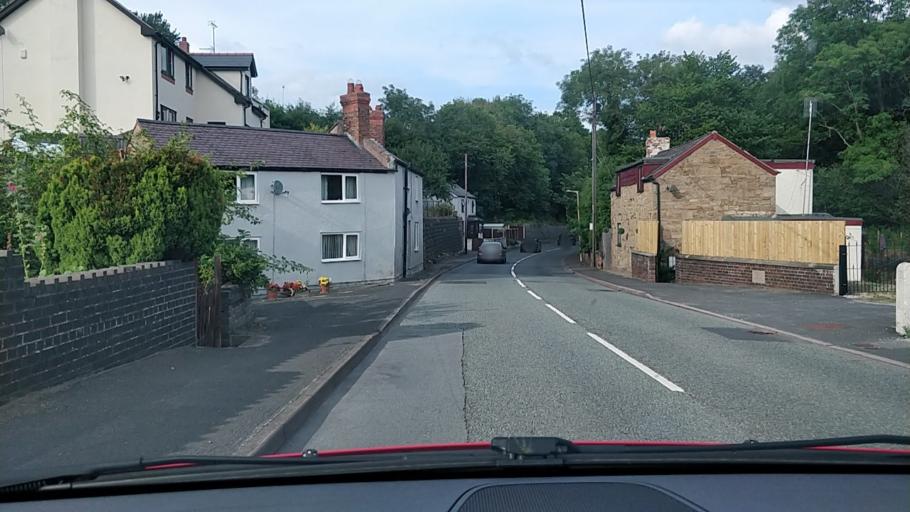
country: GB
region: Wales
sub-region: County of Flintshire
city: Leeswood
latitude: 53.1262
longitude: -3.0900
